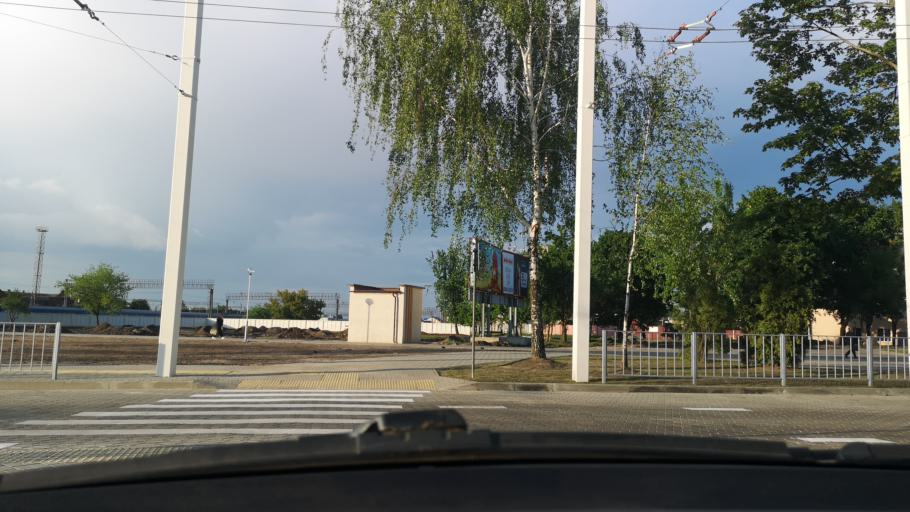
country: BY
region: Brest
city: Brest
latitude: 52.0990
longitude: 23.6835
